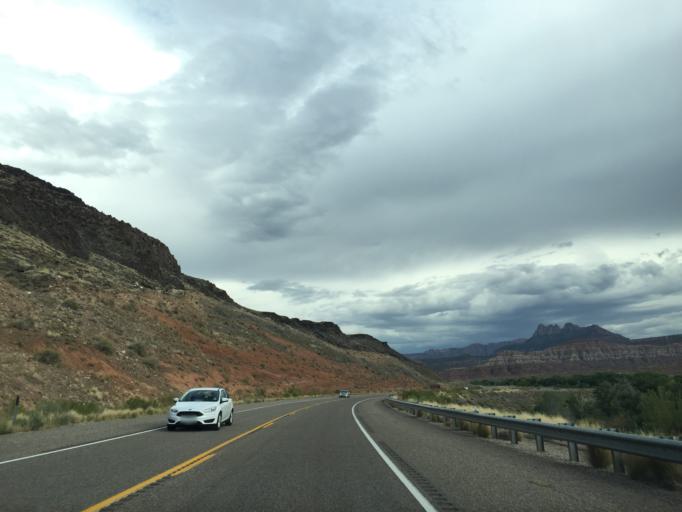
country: US
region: Utah
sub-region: Washington County
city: LaVerkin
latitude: 37.1942
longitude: -113.1464
